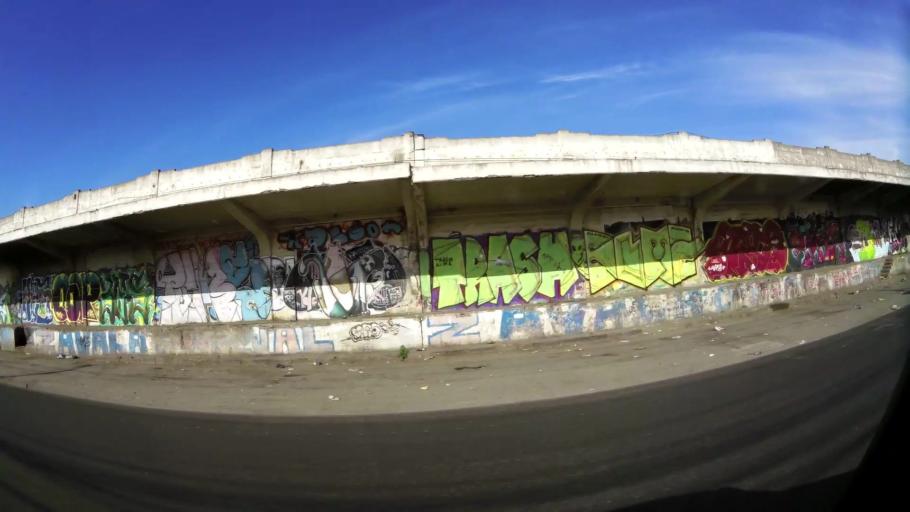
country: CL
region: Santiago Metropolitan
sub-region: Provincia de Santiago
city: Santiago
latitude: -33.4601
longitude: -70.6811
